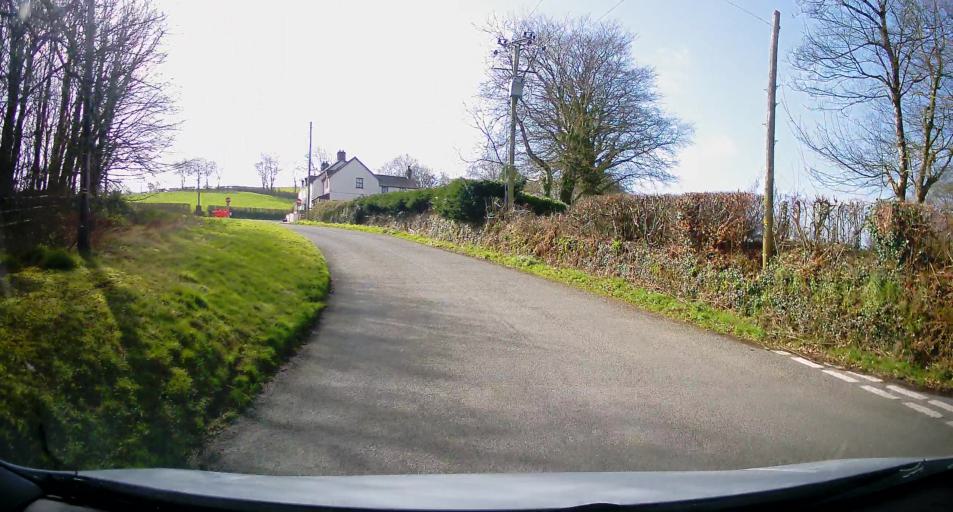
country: GB
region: Wales
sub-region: County of Ceredigion
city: Aberporth
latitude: 52.0821
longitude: -4.5439
